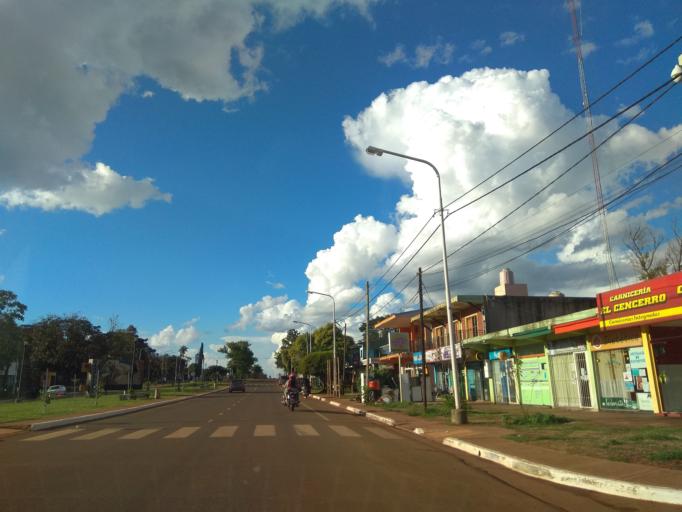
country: AR
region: Misiones
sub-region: Departamento de Candelaria
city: Candelaria
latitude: -27.4640
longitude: -55.7450
